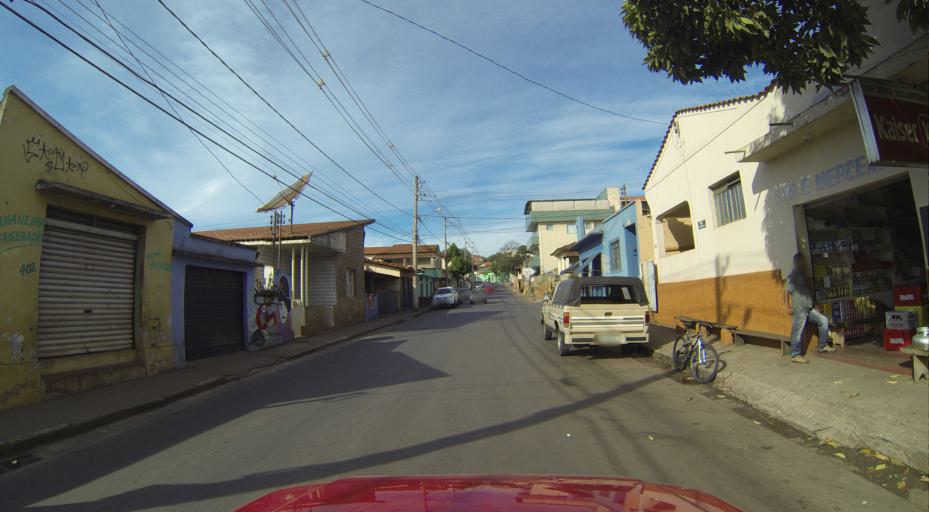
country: BR
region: Minas Gerais
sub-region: Brumadinho
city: Brumadinho
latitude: -20.1426
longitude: -44.2078
